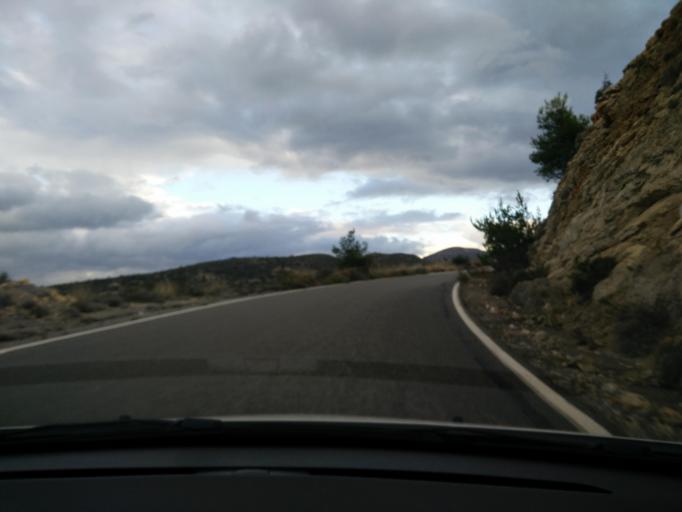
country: GR
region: Crete
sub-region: Nomos Lasithiou
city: Gra Liyia
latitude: 35.0908
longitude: 25.6951
